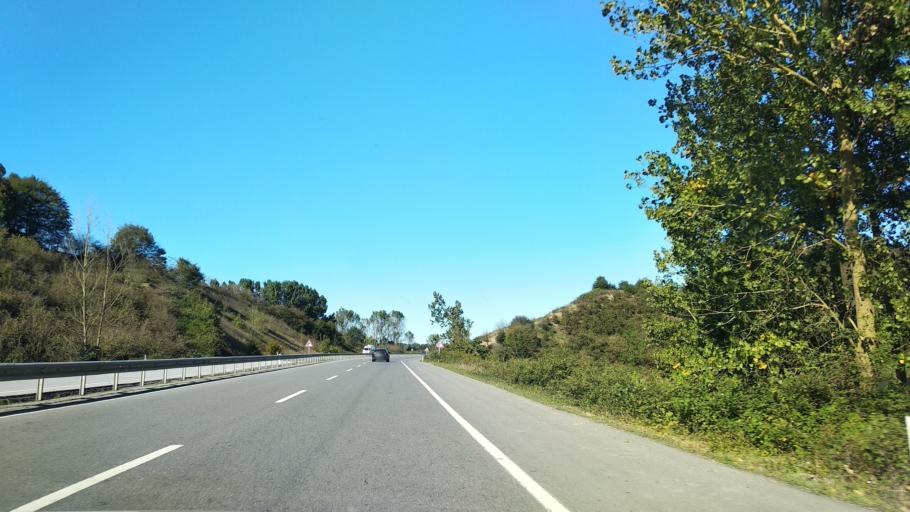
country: TR
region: Sakarya
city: Karasu
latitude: 41.0590
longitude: 30.6369
